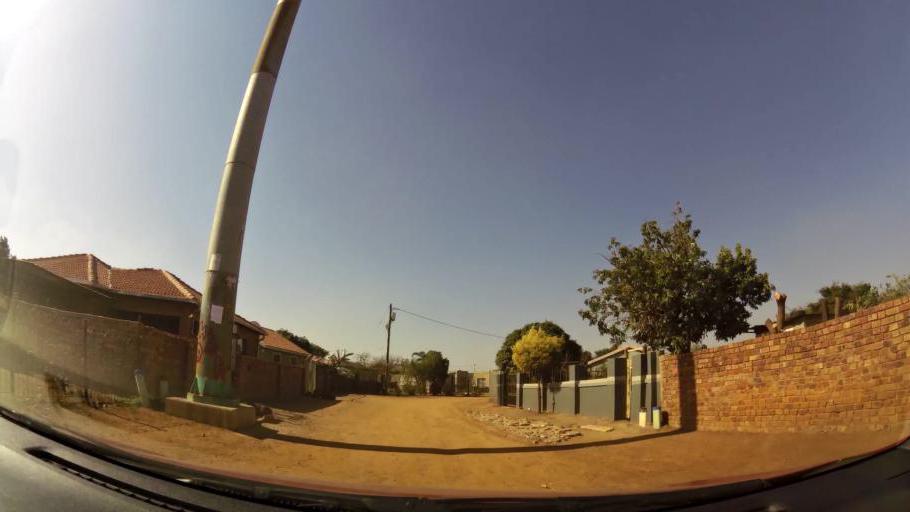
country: ZA
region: Gauteng
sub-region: City of Tshwane Metropolitan Municipality
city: Mabopane
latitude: -25.5493
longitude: 28.0863
